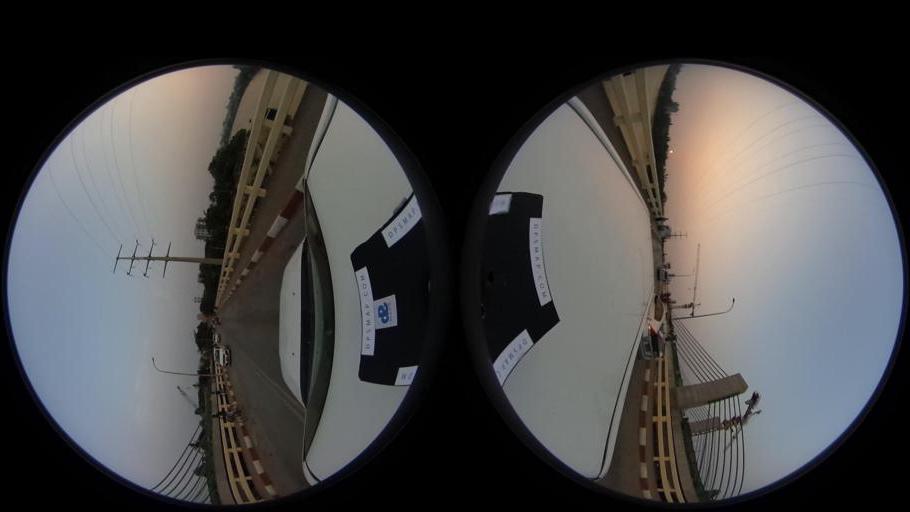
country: MM
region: Yangon
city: Yangon
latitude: 16.7849
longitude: 96.1792
